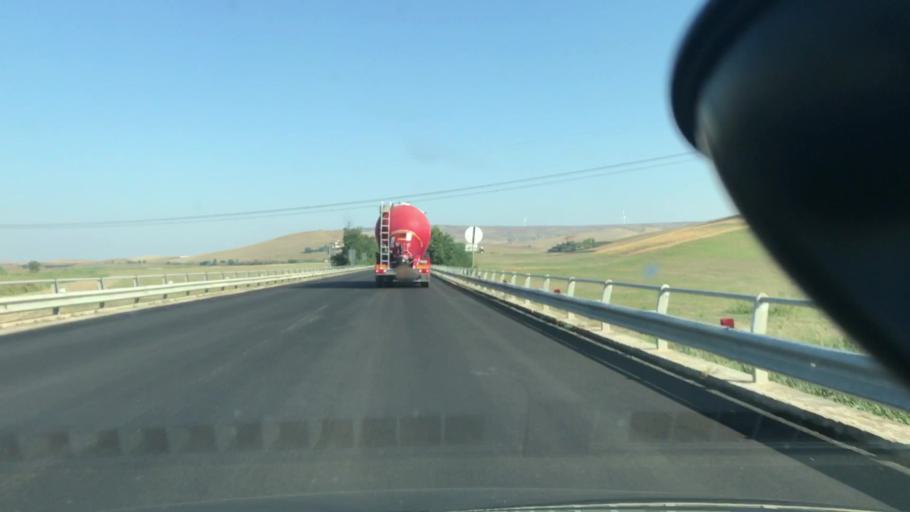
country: IT
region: Basilicate
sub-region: Provincia di Matera
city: Irsina
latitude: 40.7979
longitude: 16.2751
